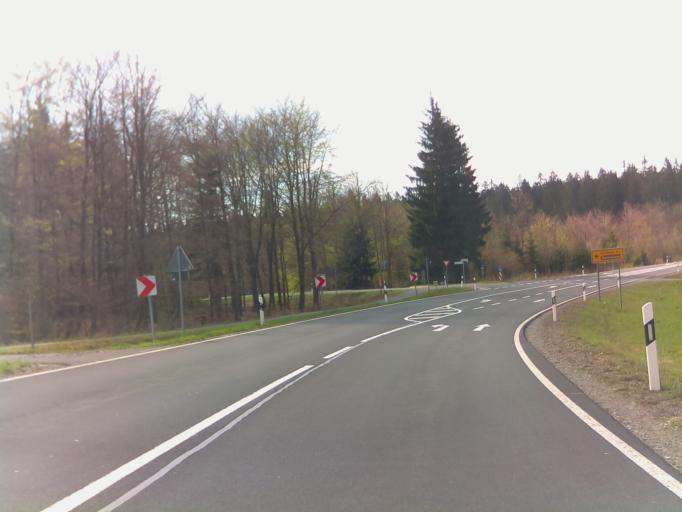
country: DE
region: Bavaria
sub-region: Upper Franconia
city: Ludwigsstadt
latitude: 50.4505
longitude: 11.3532
